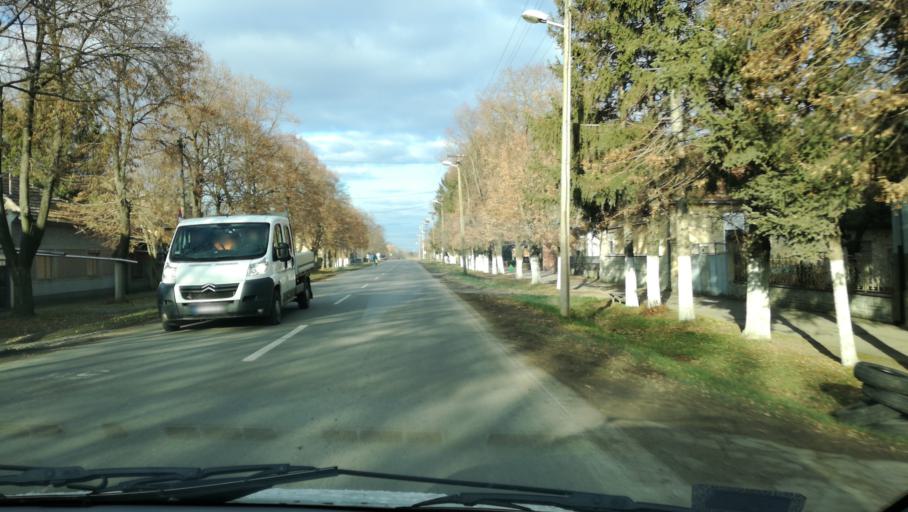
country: RS
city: Tiszahegyes
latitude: 45.8237
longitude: 20.3126
